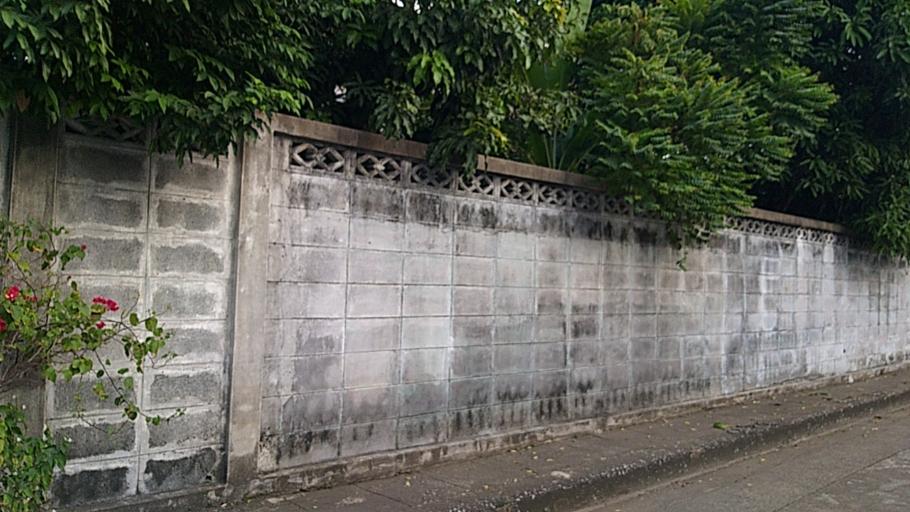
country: TH
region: Bangkok
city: Lat Phrao
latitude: 13.8262
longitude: 100.6076
